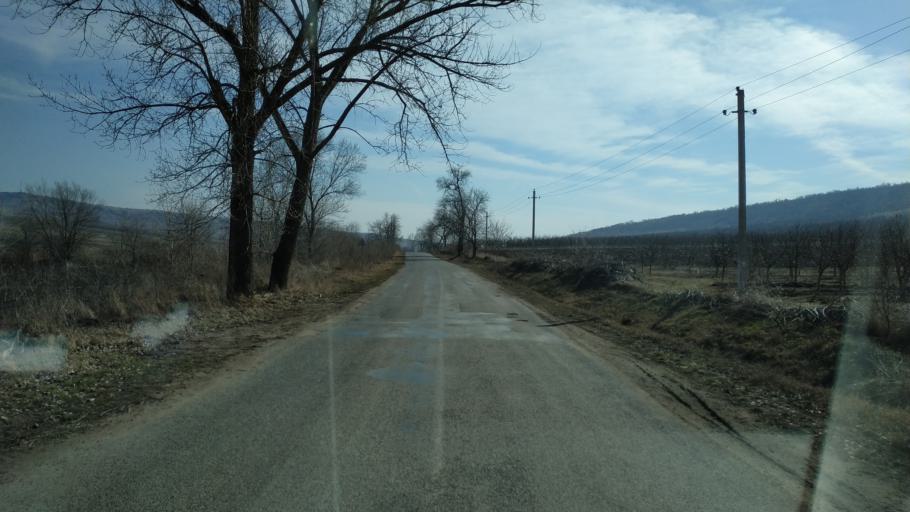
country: MD
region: Nisporeni
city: Nisporeni
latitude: 47.1462
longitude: 28.1099
